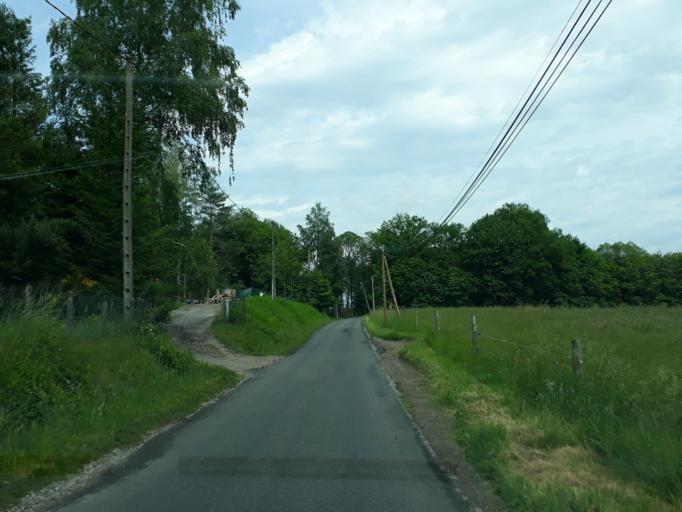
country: FR
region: Limousin
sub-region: Departement de la Correze
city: Beynat
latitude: 45.1172
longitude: 1.7540
